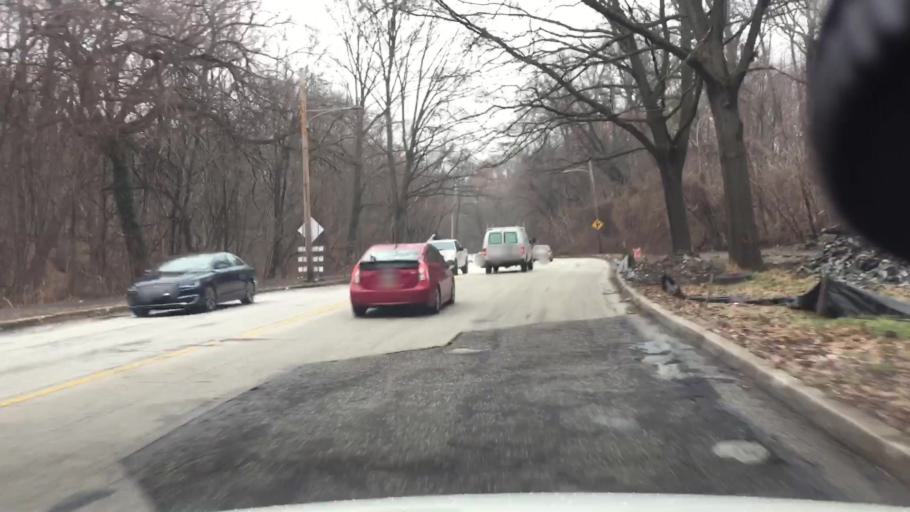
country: US
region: Pennsylvania
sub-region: Montgomery County
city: Wyndmoor
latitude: 40.0333
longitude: -75.1878
